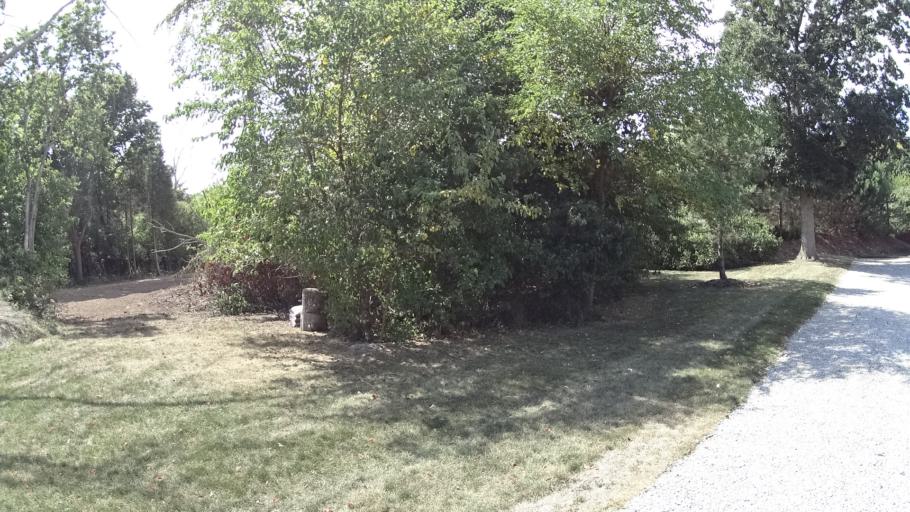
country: US
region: Ohio
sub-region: Erie County
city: Sandusky
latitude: 41.6098
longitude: -82.6931
